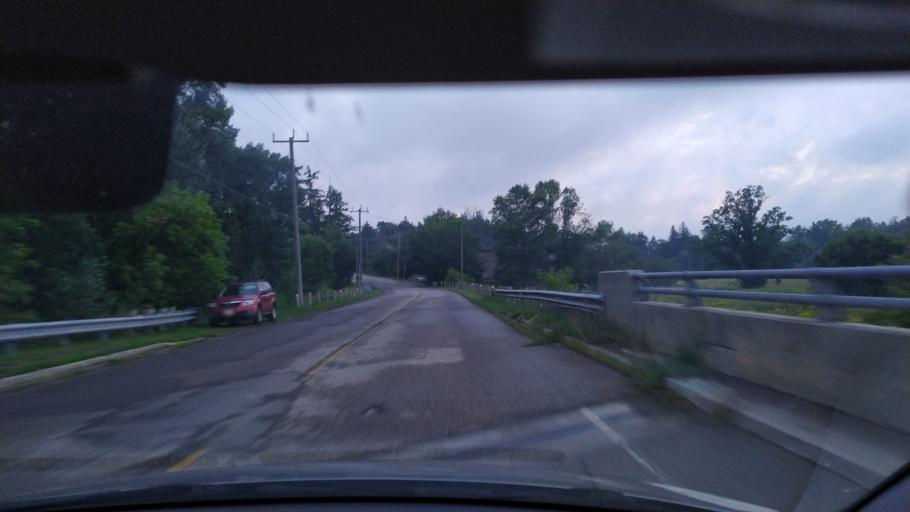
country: CA
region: Ontario
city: Kitchener
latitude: 43.3552
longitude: -80.6655
